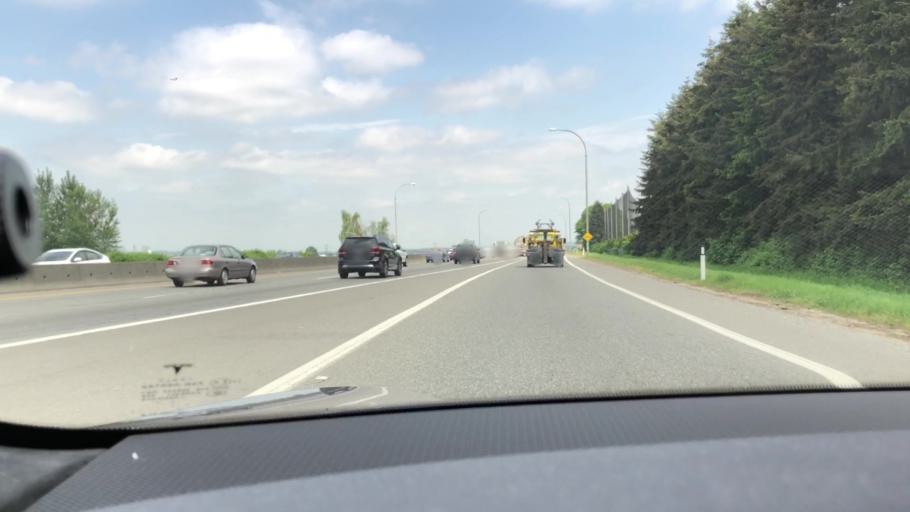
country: CA
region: British Columbia
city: Richmond
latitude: 49.1777
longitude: -123.0649
